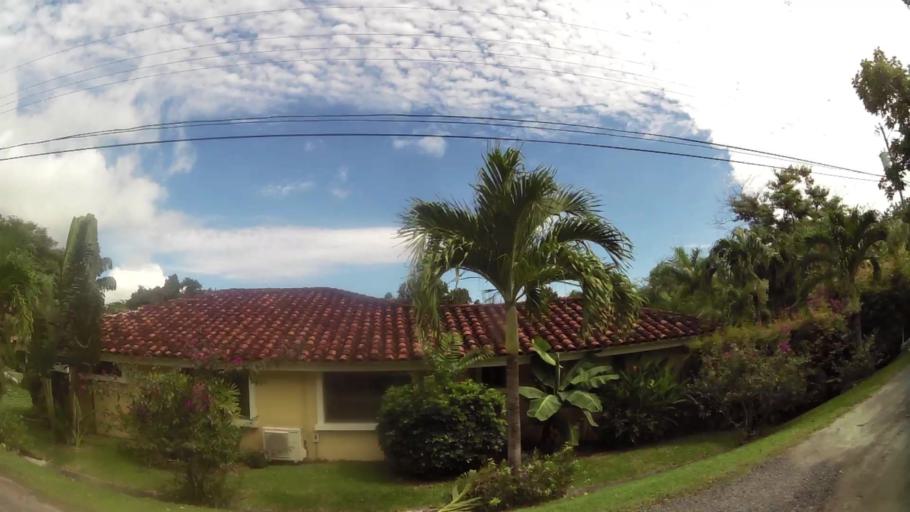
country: PA
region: Panama
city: Nueva Gorgona
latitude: 8.5401
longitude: -79.9048
